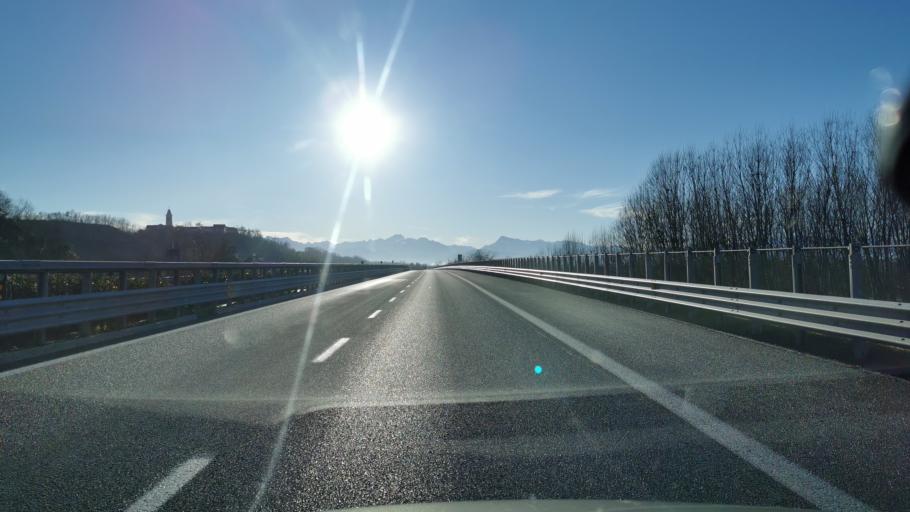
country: IT
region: Piedmont
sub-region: Provincia di Cuneo
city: Montanera
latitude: 44.4703
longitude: 7.6699
